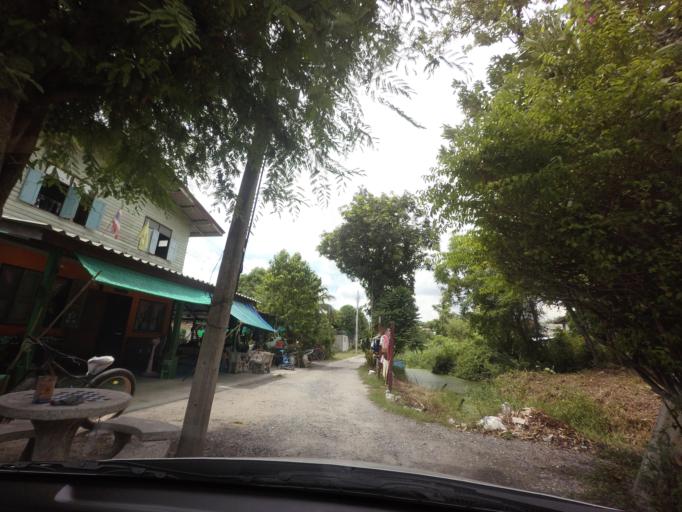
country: TH
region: Nonthaburi
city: Mueang Nonthaburi
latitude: 13.8885
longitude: 100.5173
